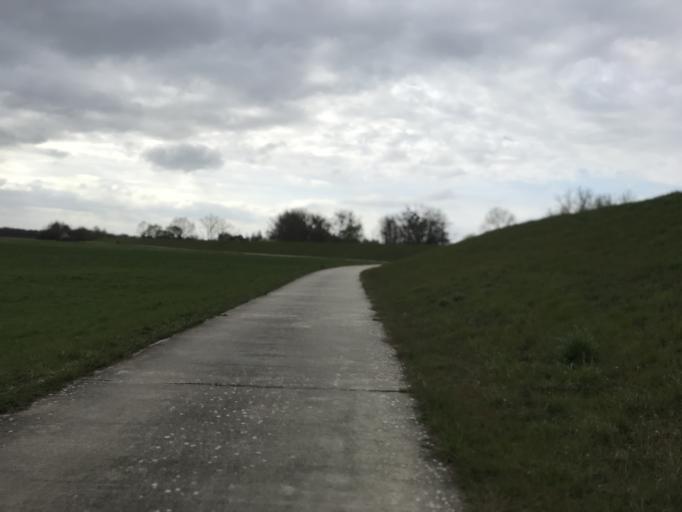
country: DE
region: Rheinland-Pfalz
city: Oppenheim
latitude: 49.8484
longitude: 8.3992
